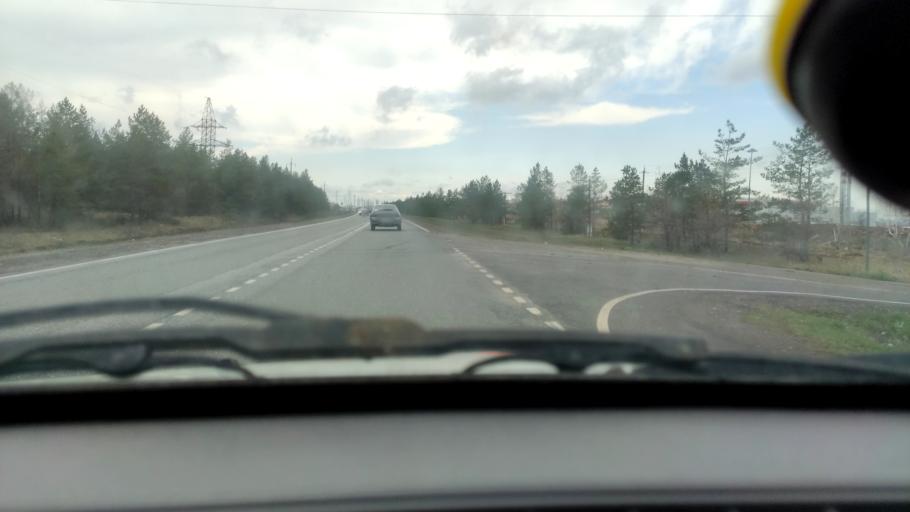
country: RU
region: Samara
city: Zhigulevsk
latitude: 53.5722
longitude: 49.5530
